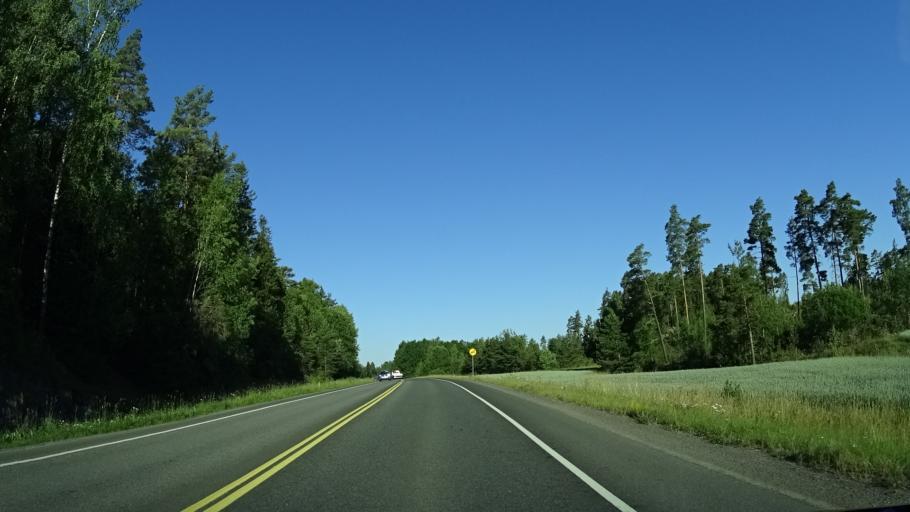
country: FI
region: Varsinais-Suomi
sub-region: Turku
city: Naantali
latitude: 60.4603
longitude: 21.9766
